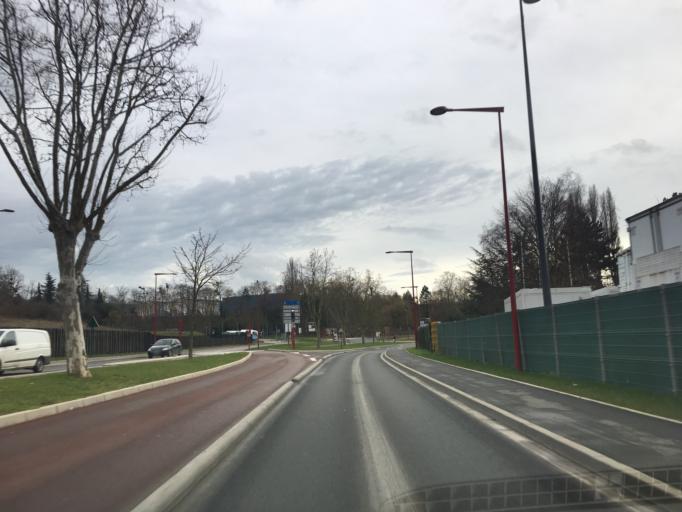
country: FR
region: Ile-de-France
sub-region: Departement du Val-d'Oise
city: Gonesse
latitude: 48.9870
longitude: 2.4594
